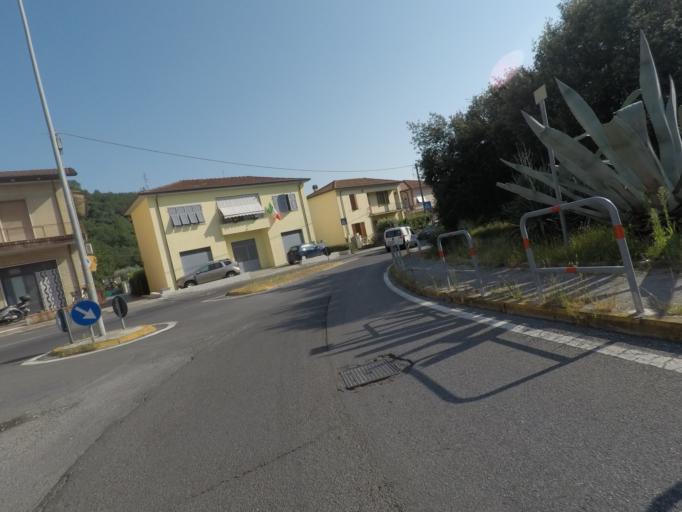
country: IT
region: Liguria
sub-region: Provincia di La Spezia
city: Casano-Dogana-Isola
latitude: 44.0812
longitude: 10.0345
